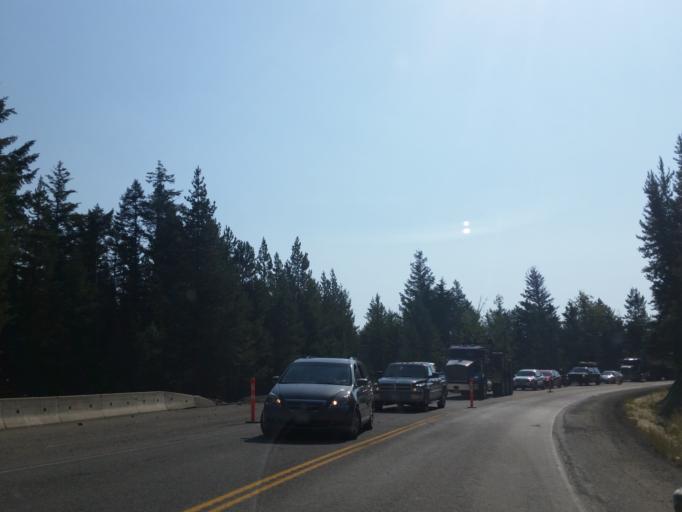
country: CA
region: British Columbia
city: Princeton
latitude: 49.2778
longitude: -120.5771
